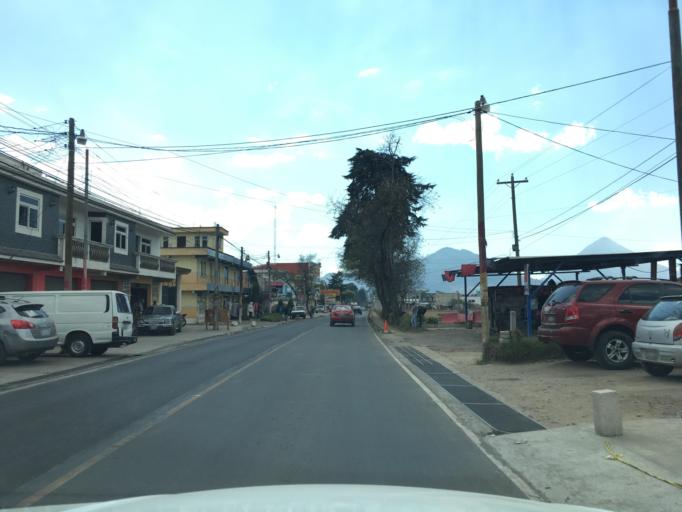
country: GT
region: Quetzaltenango
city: Olintepeque
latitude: 14.8759
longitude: -91.5137
